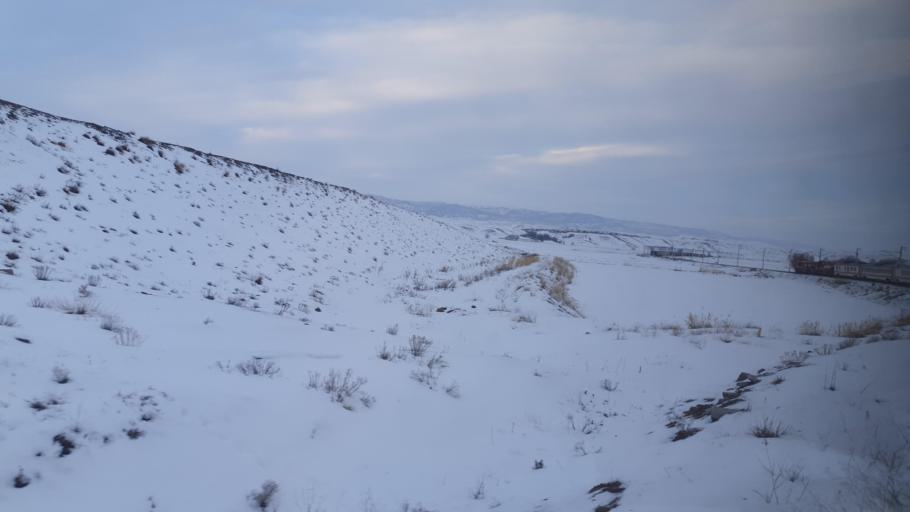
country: TR
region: Yozgat
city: Yerkoy
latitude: 39.6873
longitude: 34.4123
